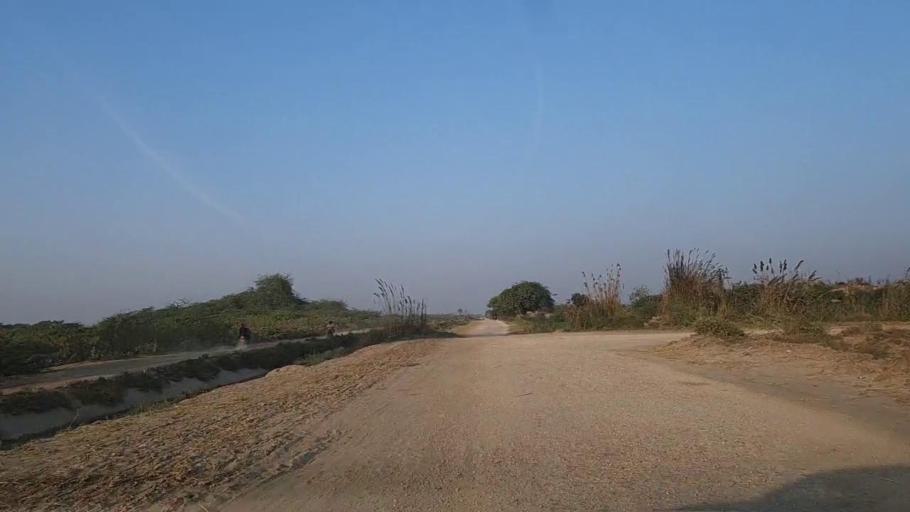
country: PK
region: Sindh
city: Keti Bandar
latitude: 24.2728
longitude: 67.6817
